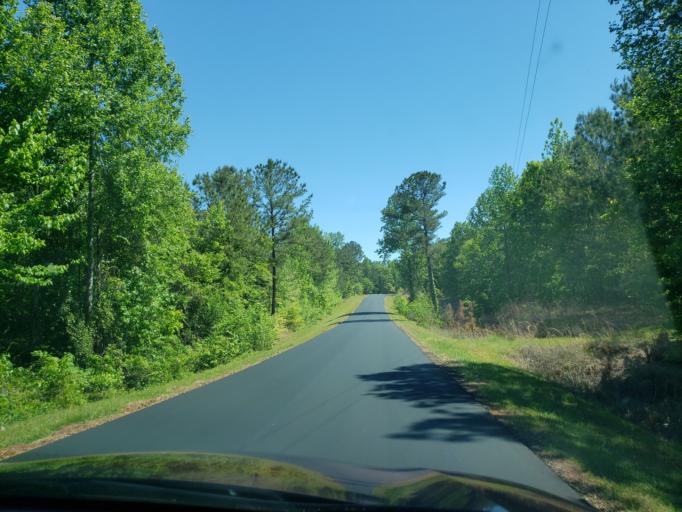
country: US
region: Alabama
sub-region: Elmore County
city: Eclectic
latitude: 32.7051
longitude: -85.8829
